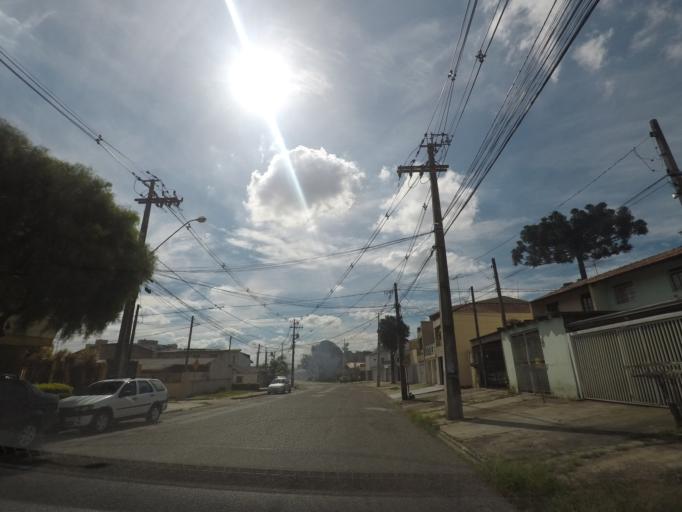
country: BR
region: Parana
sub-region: Curitiba
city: Curitiba
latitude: -25.4943
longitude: -49.2707
